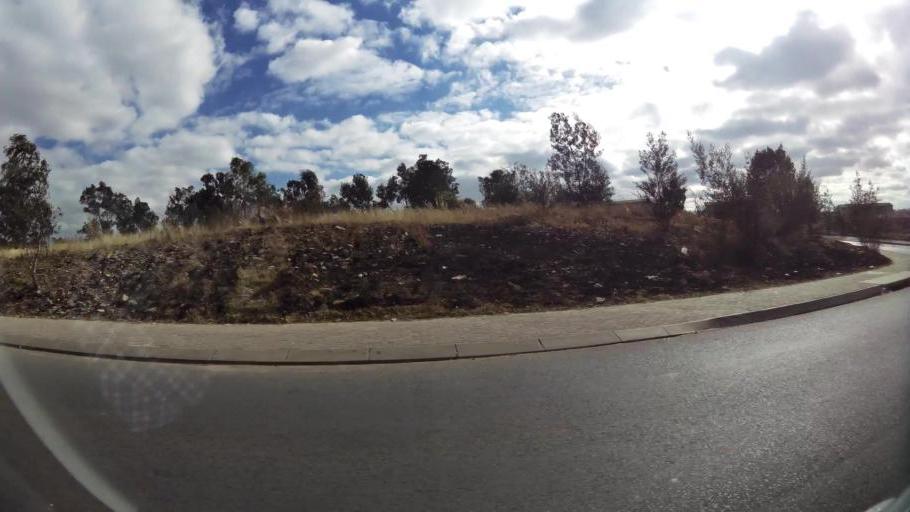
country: ZA
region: Gauteng
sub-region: City of Johannesburg Metropolitan Municipality
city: Roodepoort
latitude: -26.1934
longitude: 27.9032
